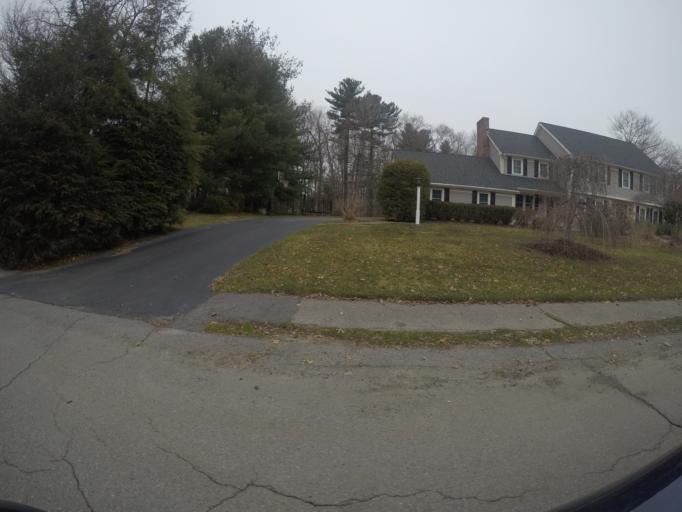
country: US
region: Massachusetts
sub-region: Bristol County
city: Easton
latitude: 42.0562
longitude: -71.1449
